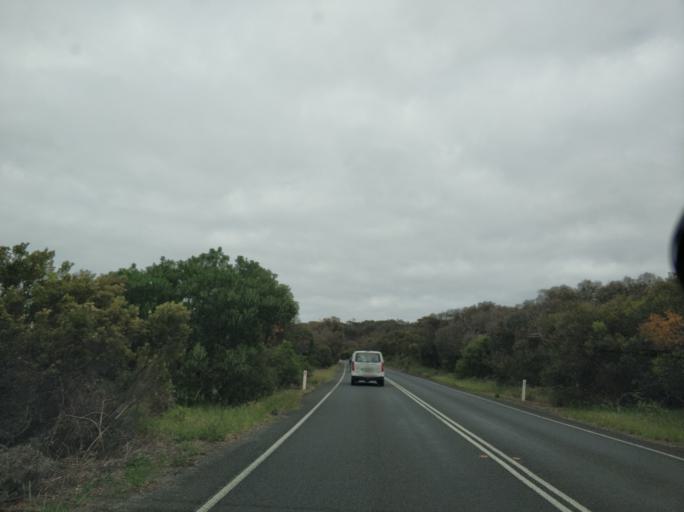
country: AU
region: Victoria
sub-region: Surf Coast
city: Anglesea
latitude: -38.4341
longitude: 144.1308
